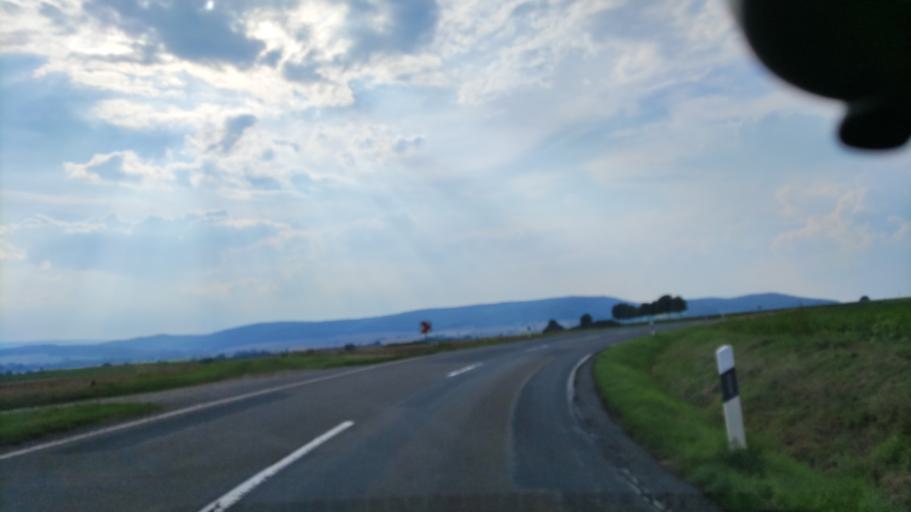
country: DE
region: Lower Saxony
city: Eimen
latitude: 51.8362
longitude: 9.7535
